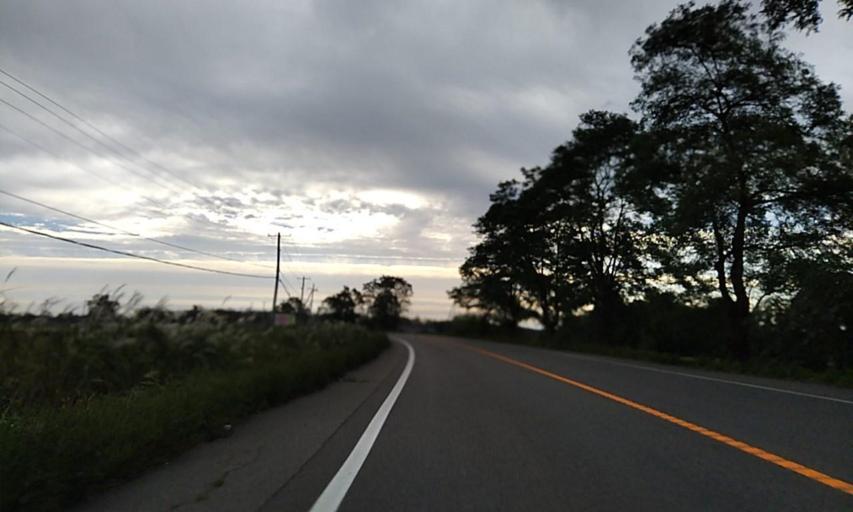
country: JP
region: Hokkaido
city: Obihiro
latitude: 42.9184
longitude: 142.9996
